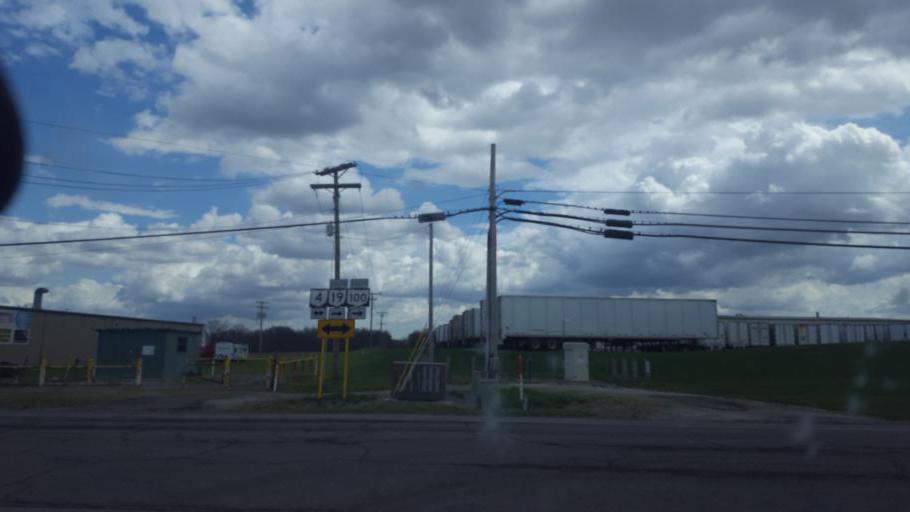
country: US
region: Ohio
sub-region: Crawford County
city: Bucyrus
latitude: 40.8341
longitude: -82.9715
